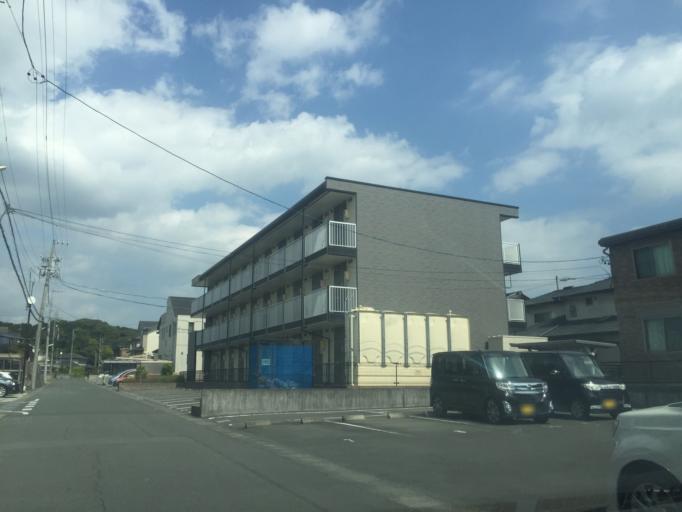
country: JP
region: Shizuoka
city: Kakegawa
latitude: 34.7814
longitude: 138.0026
